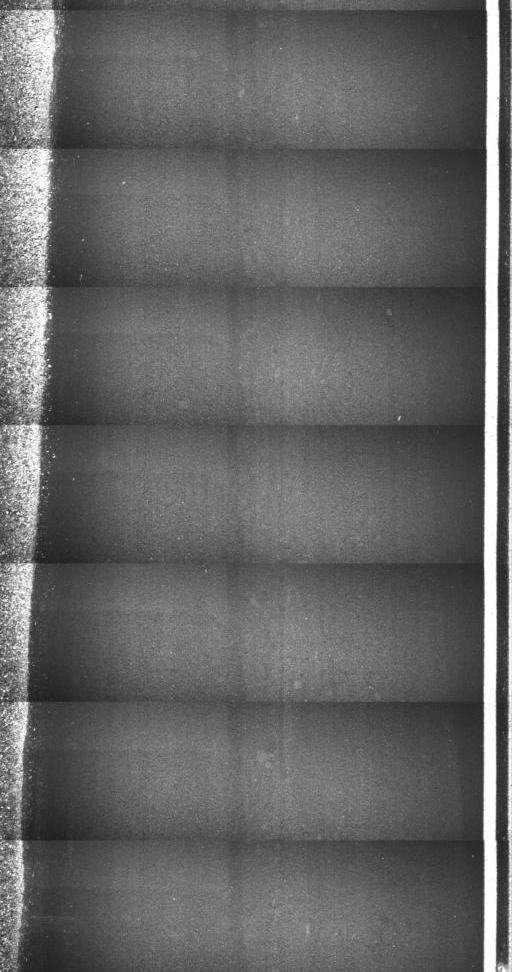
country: US
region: Vermont
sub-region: Windsor County
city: Woodstock
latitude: 43.5880
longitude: -72.5155
